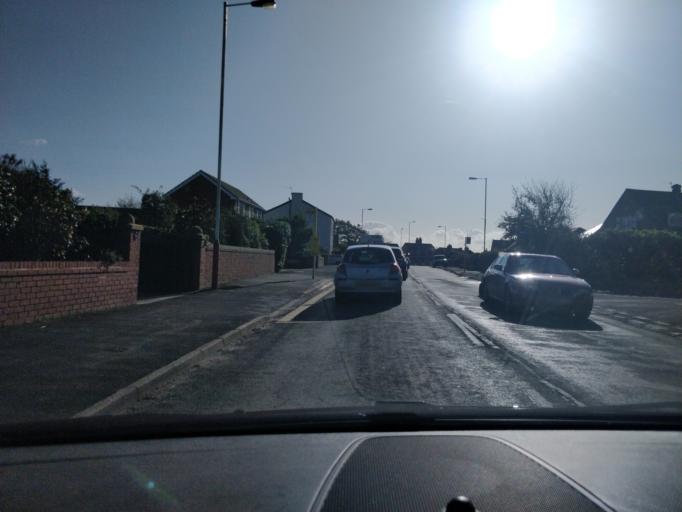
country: GB
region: England
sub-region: Lancashire
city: Banks
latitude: 53.6770
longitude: -2.9465
